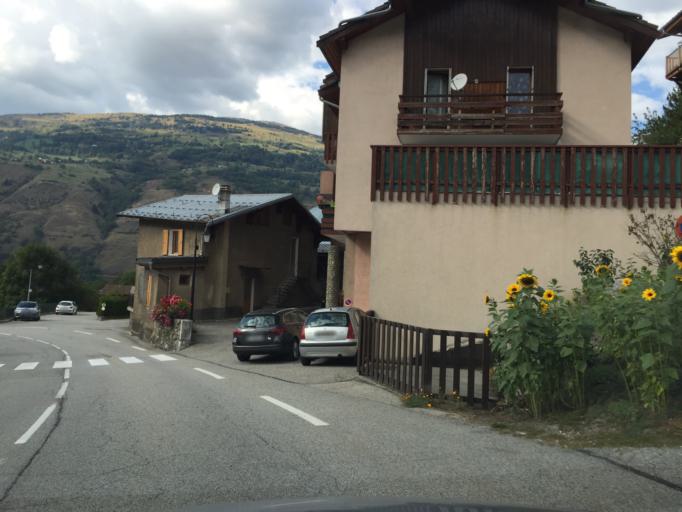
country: FR
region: Rhone-Alpes
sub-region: Departement de la Savoie
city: Bourg-Saint-Maurice
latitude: 45.5694
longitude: 6.7418
